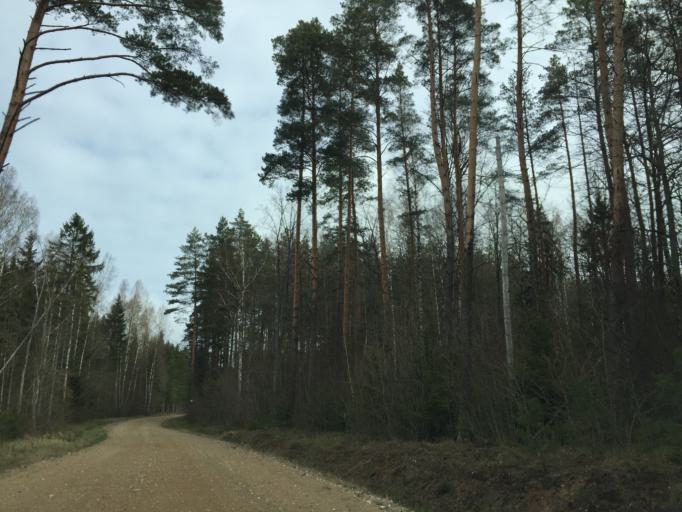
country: LV
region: Salacgrivas
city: Salacgriva
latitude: 57.5138
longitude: 24.4137
